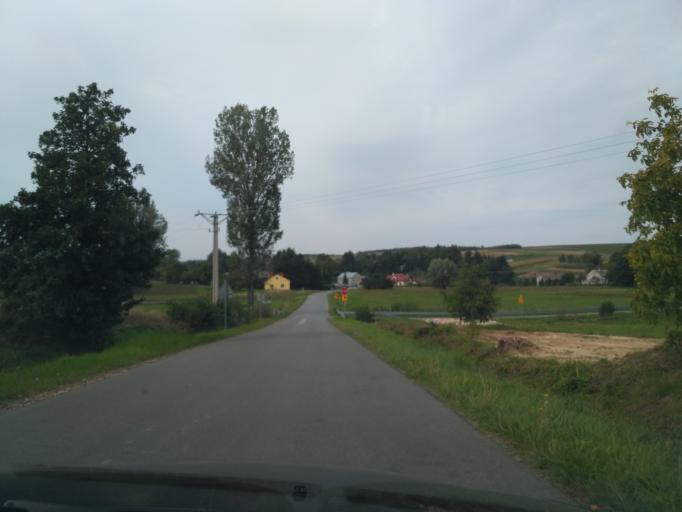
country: PL
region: Subcarpathian Voivodeship
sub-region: Powiat rzeszowski
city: Zglobien
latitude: 50.0313
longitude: 21.8437
